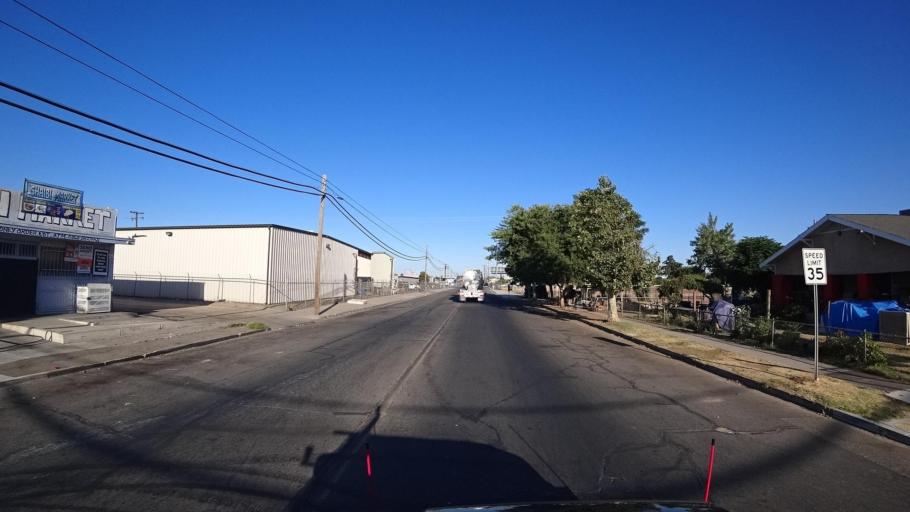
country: US
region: California
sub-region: Fresno County
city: Fresno
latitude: 36.7069
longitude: -119.7586
